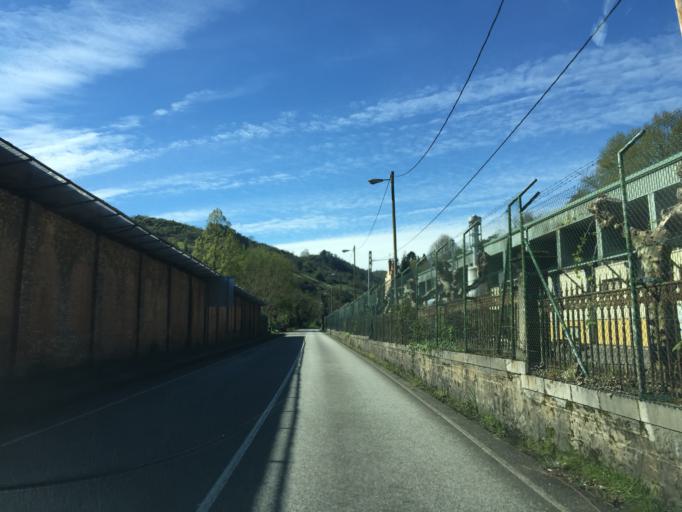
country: ES
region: Asturias
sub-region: Province of Asturias
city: Castandiello
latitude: 43.3504
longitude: -5.9691
